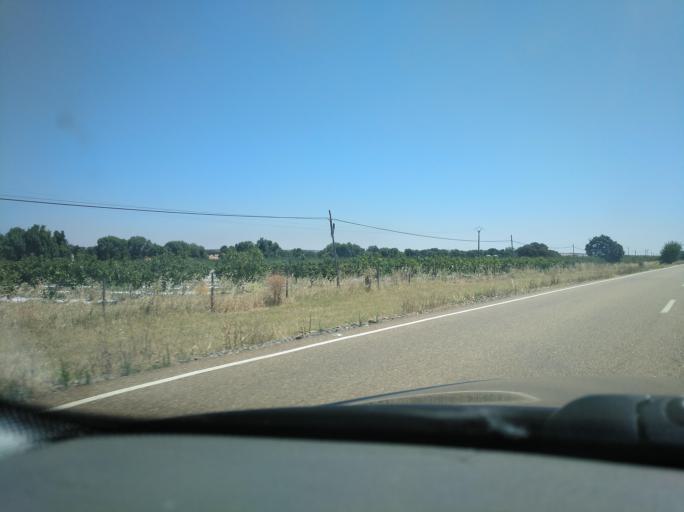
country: ES
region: Extremadura
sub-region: Provincia de Badajoz
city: Olivenza
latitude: 38.7047
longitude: -7.1698
